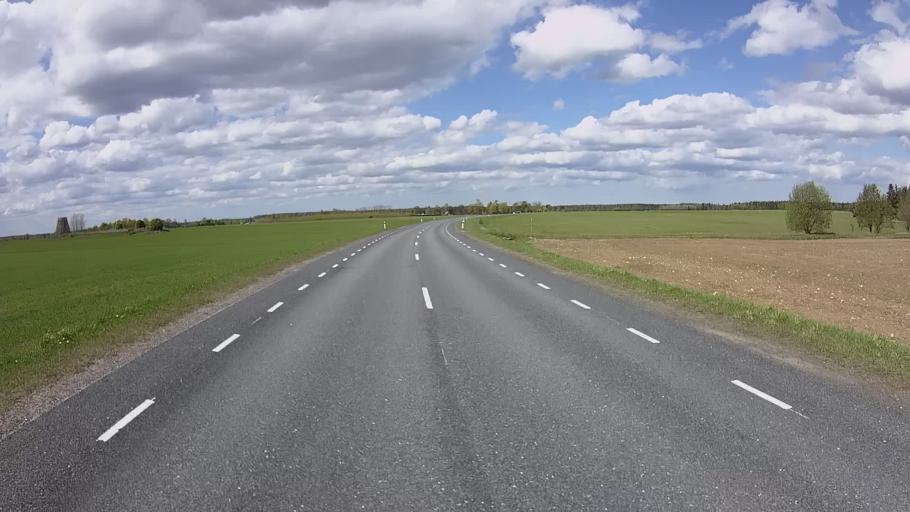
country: EE
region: Jaervamaa
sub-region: Jaerva-Jaani vald
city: Jarva-Jaani
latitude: 59.1102
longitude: 25.7987
